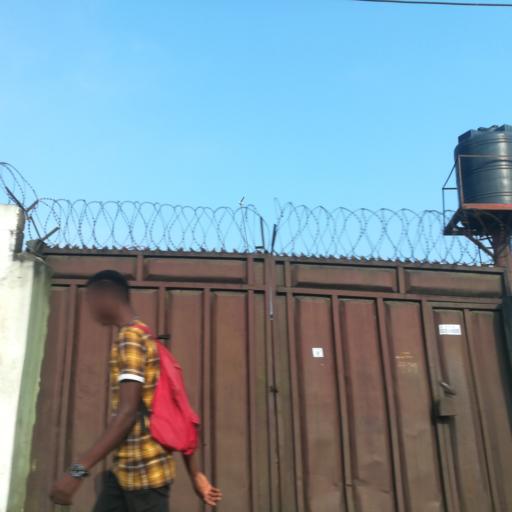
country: NG
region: Rivers
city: Port Harcourt
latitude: 4.8572
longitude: 6.9653
